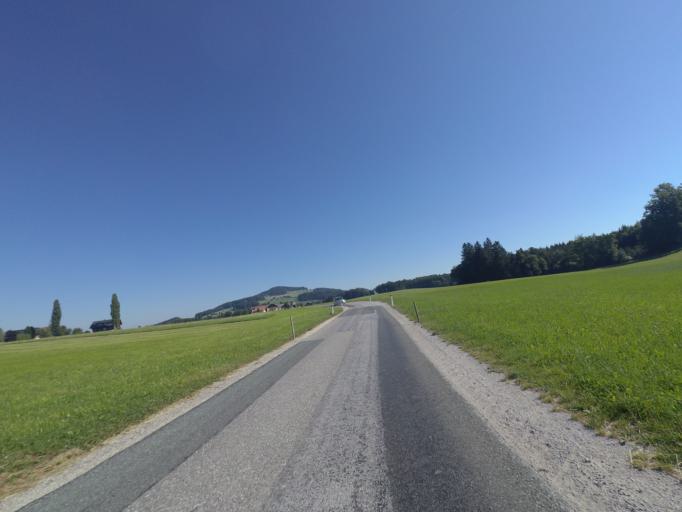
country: AT
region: Salzburg
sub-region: Politischer Bezirk Salzburg-Umgebung
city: Obertrum am See
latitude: 47.9279
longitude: 13.1056
